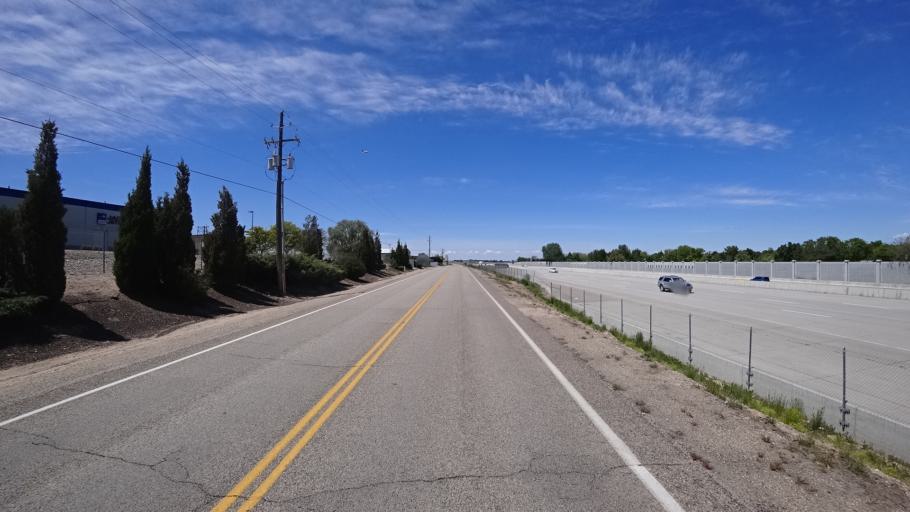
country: US
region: Idaho
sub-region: Ada County
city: Boise
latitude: 43.5717
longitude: -116.2292
